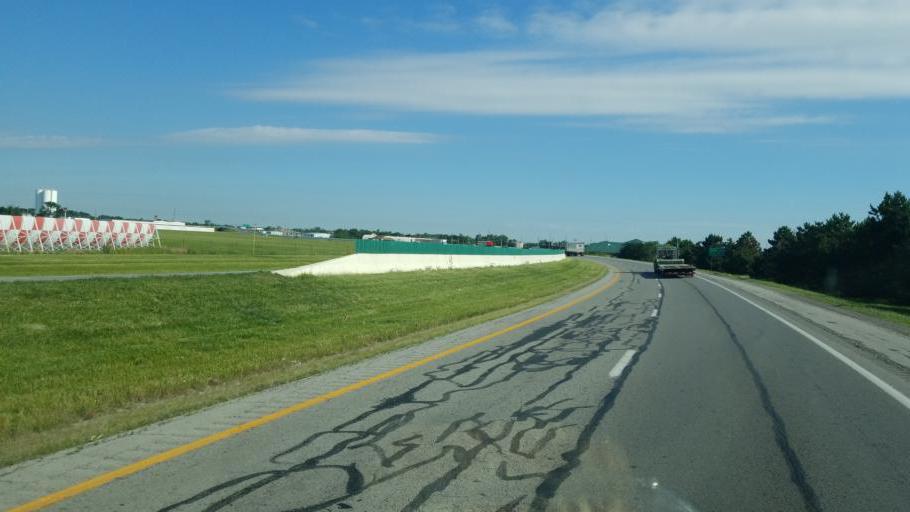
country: US
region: Ohio
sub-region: Hancock County
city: Findlay
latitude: 41.0170
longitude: -83.6604
